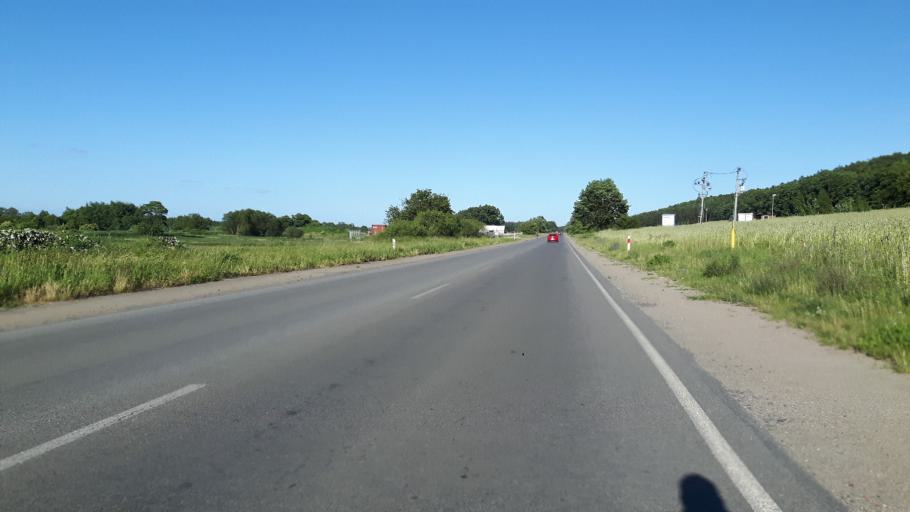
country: PL
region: Pomeranian Voivodeship
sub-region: Powiat pucki
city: Mrzezino
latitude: 54.6051
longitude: 18.4316
